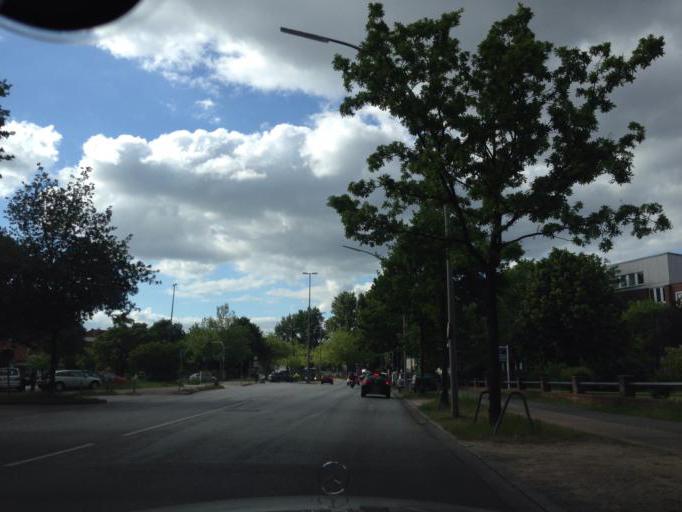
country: DE
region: Hamburg
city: Barmbek-Nord
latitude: 53.5858
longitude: 10.0523
